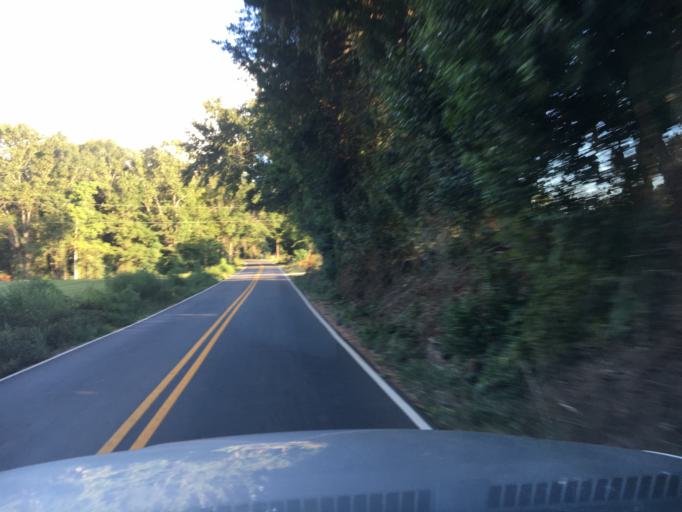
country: US
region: South Carolina
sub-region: Spartanburg County
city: Roebuck
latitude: 34.8943
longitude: -82.0295
